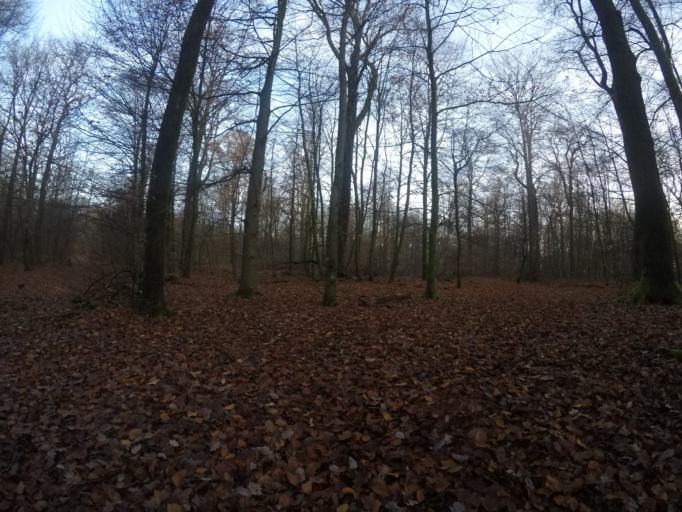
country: BE
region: Wallonia
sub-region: Province du Luxembourg
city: Habay-la-Vieille
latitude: 49.7467
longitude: 5.6726
